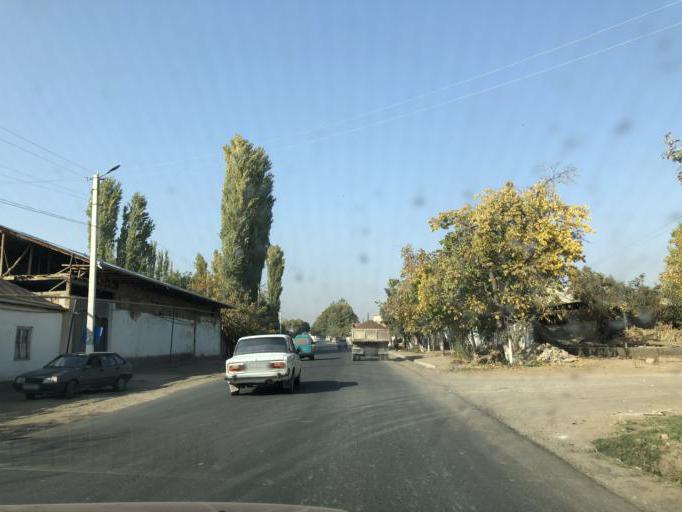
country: UZ
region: Namangan
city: Chust Shahri
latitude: 41.0704
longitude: 71.2046
